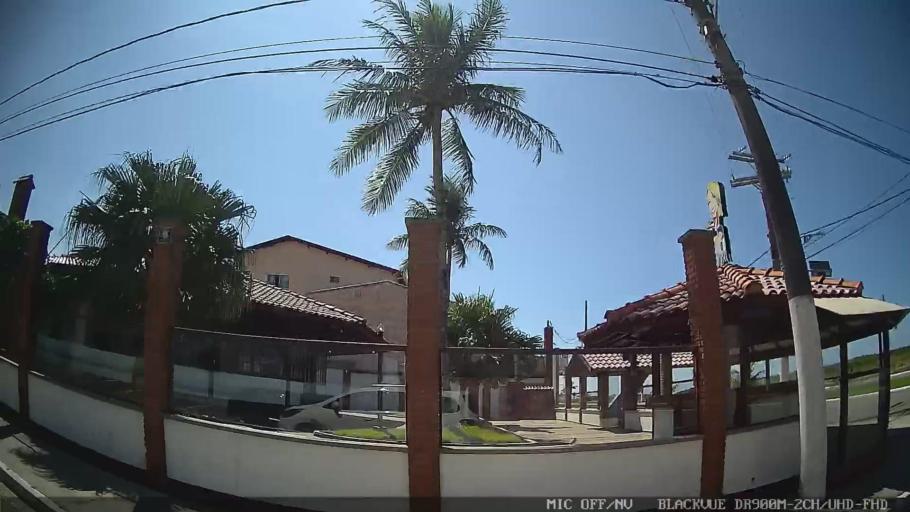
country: BR
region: Sao Paulo
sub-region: Peruibe
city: Peruibe
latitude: -24.3280
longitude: -47.0000
